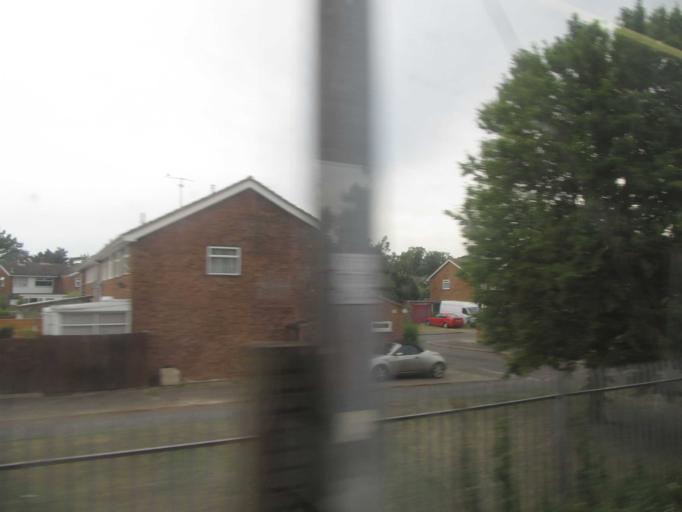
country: GB
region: England
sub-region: Bedford
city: Elstow
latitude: 52.1151
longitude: -0.4793
